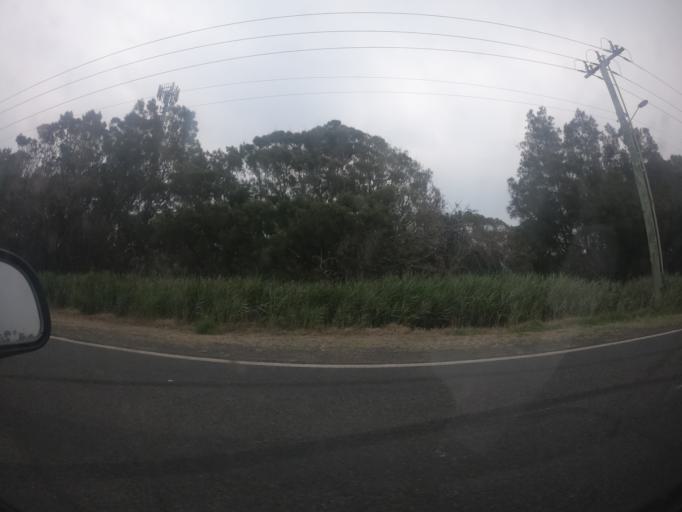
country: AU
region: New South Wales
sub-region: Shellharbour
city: Barrack Heights
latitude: -34.5683
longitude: 150.8665
